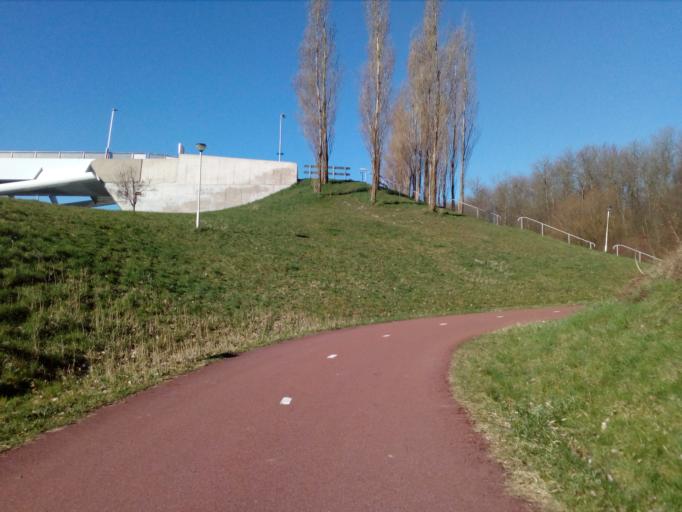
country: NL
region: South Holland
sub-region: Gemeente Zoetermeer
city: Zoetermeer
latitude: 52.0498
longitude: 4.4612
